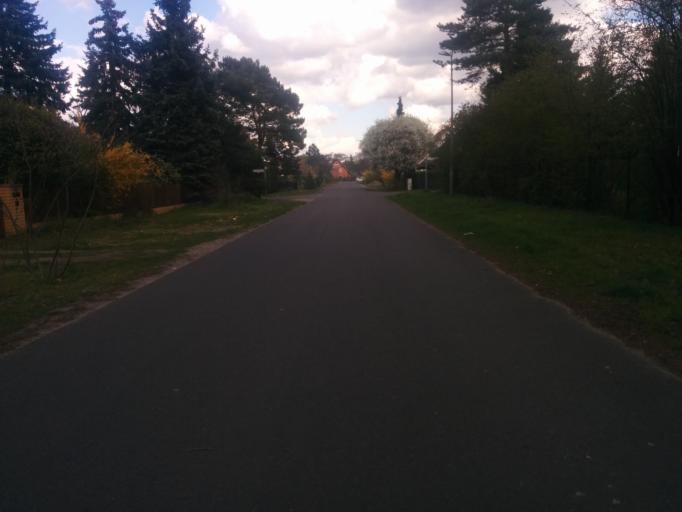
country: DE
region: Berlin
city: Biesdorf
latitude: 52.4946
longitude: 13.5517
